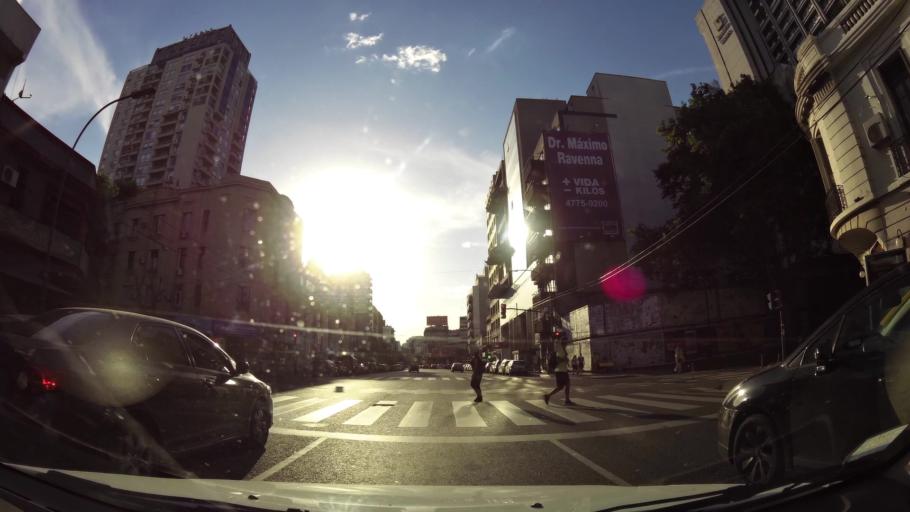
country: AR
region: Buenos Aires F.D.
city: Colegiales
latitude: -34.5978
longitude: -58.4216
